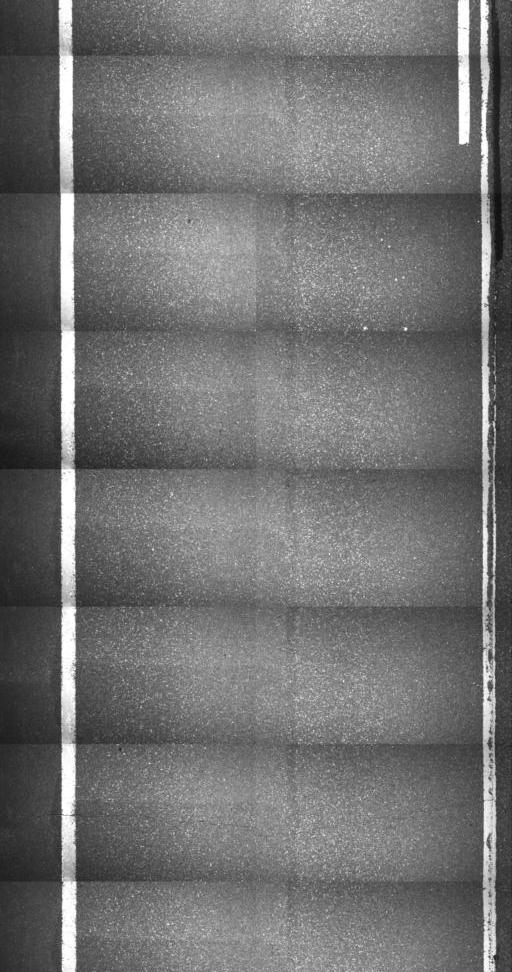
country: US
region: Vermont
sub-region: Lamoille County
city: Morrisville
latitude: 44.5099
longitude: -72.5130
